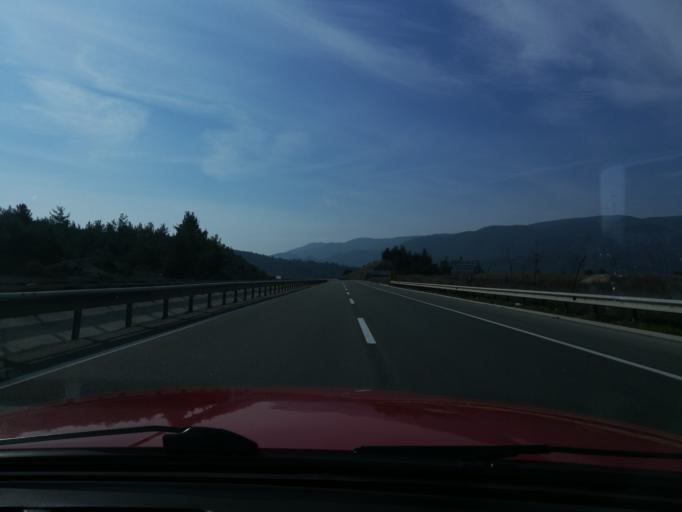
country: TR
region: Bilecik
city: Osmaneli
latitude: 40.3857
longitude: 29.9956
